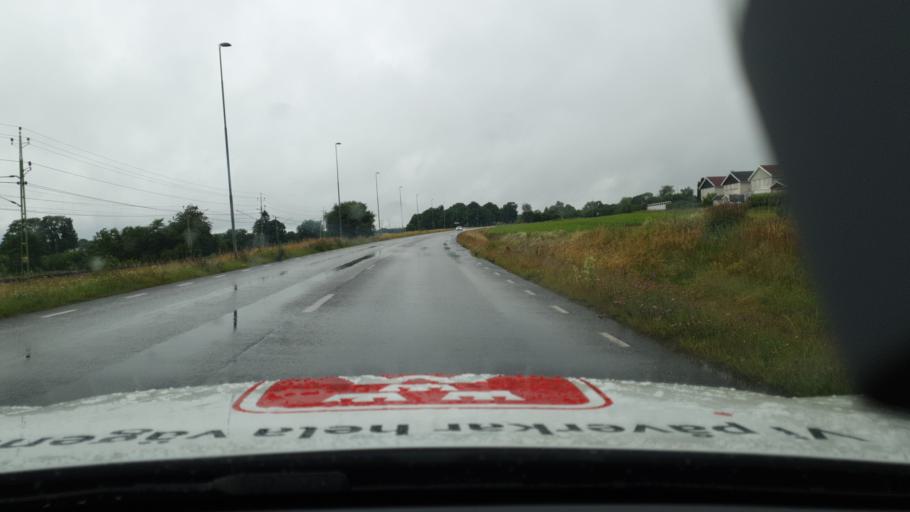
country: SE
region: Vaestra Goetaland
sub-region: Falkopings Kommun
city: Falkoeping
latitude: 58.1649
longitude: 13.5277
